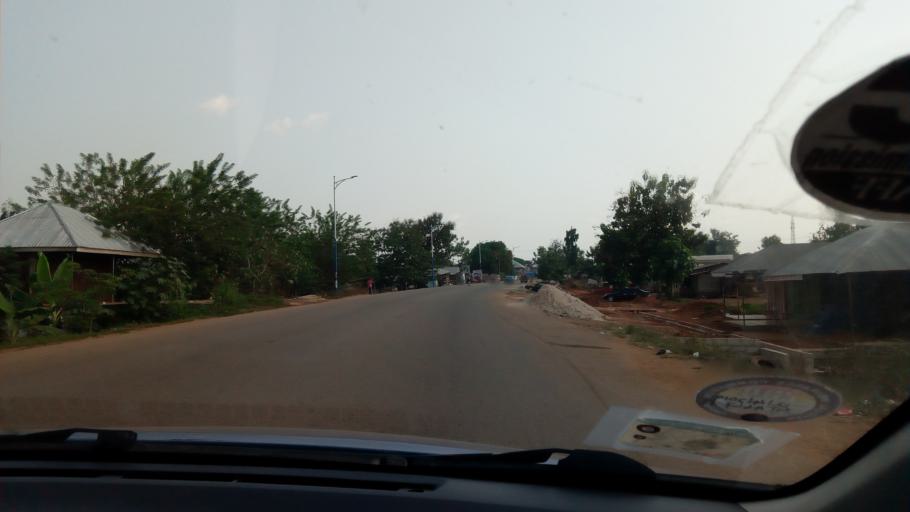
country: GH
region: Western
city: Bibiani
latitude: 6.7967
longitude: -2.5174
